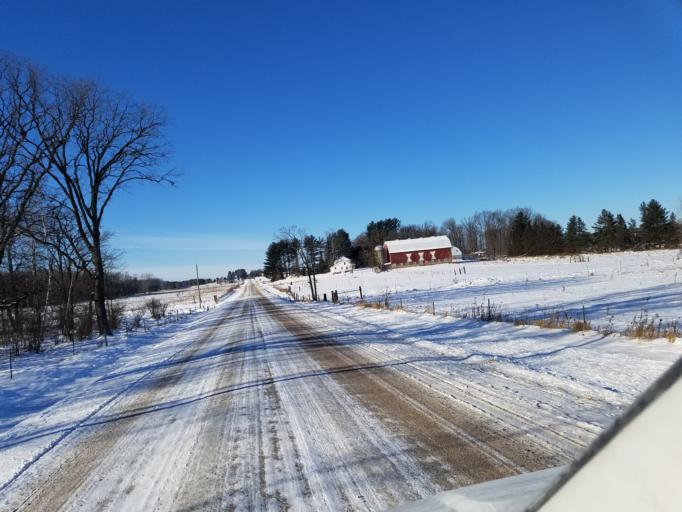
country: US
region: Wisconsin
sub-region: Clark County
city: Loyal
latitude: 44.6119
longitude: -90.3906
